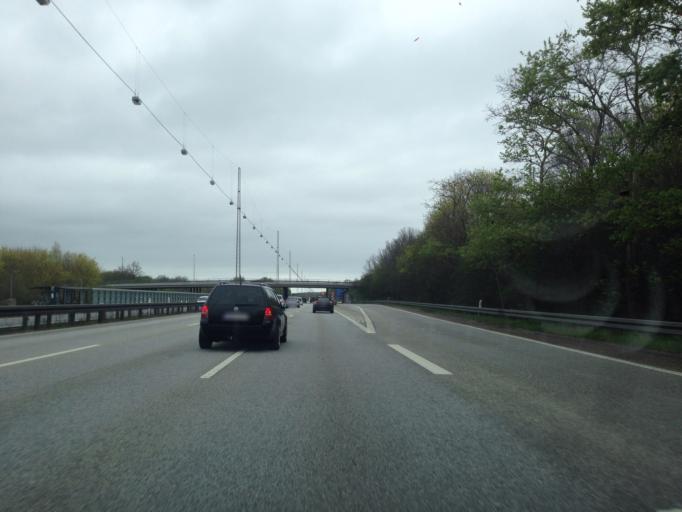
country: DK
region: Capital Region
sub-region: Lyngby-Tarbaek Kommune
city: Kongens Lyngby
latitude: 55.7861
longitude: 12.5286
